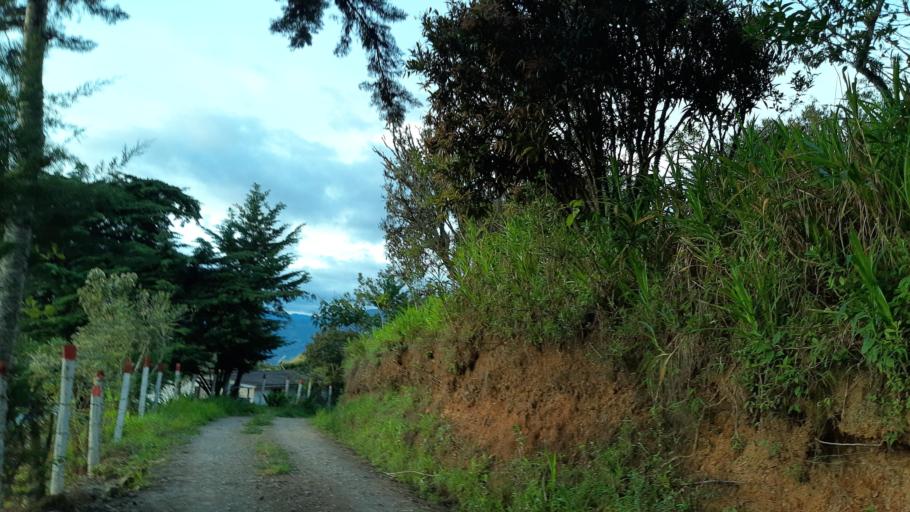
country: CO
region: Boyaca
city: Garagoa
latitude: 5.0575
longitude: -73.3778
